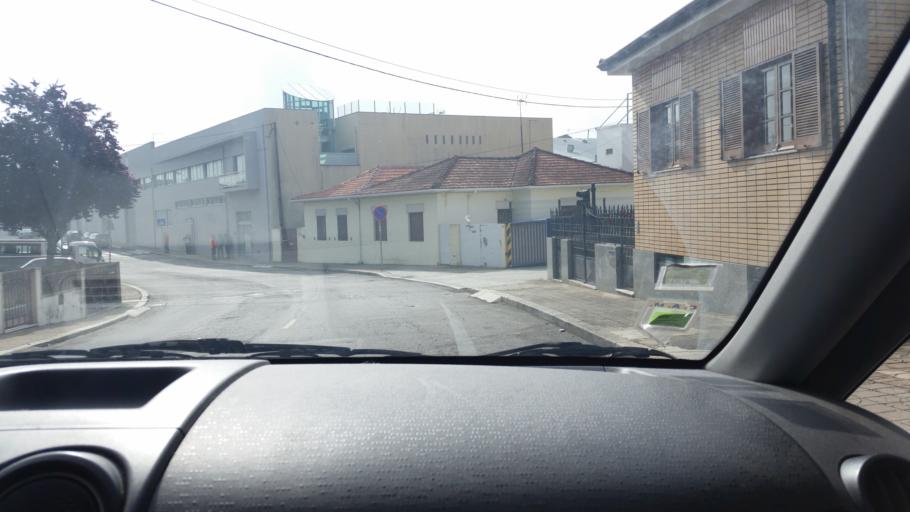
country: PT
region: Porto
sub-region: Matosinhos
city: Guifoes
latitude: 41.1993
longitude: -8.6584
